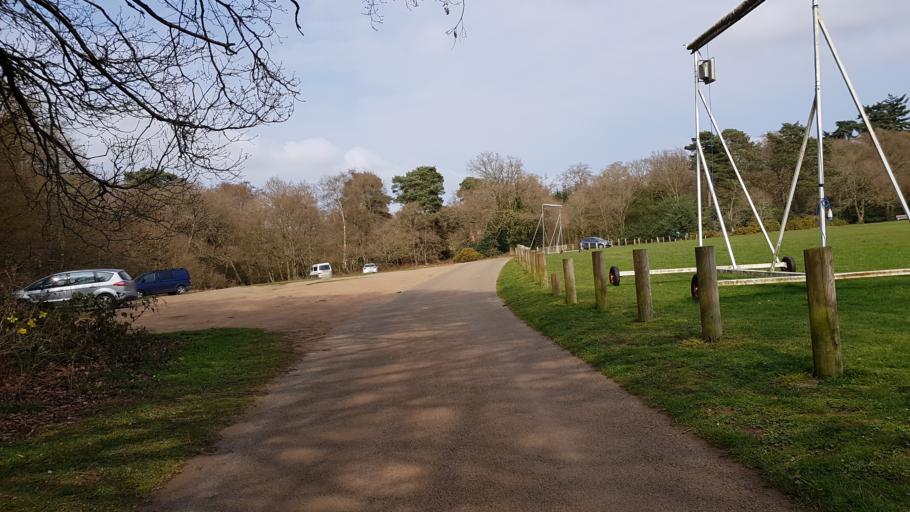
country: GB
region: England
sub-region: Surrey
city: Chilworth
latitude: 51.2120
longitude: -0.4861
